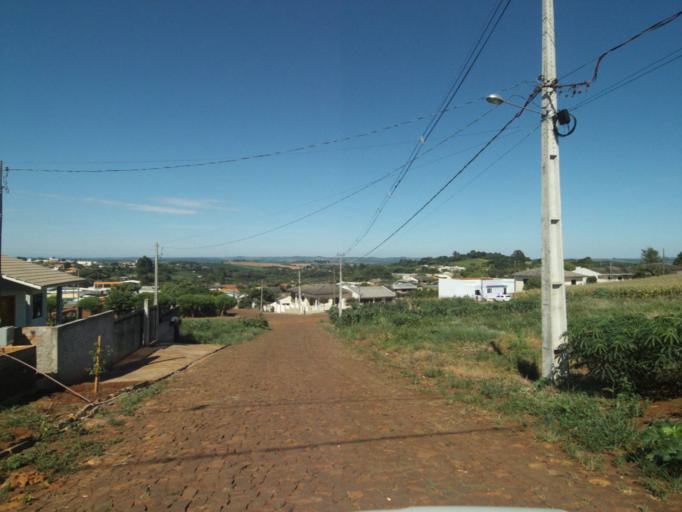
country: BR
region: Parana
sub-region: Laranjeiras Do Sul
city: Laranjeiras do Sul
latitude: -25.4864
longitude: -52.5263
